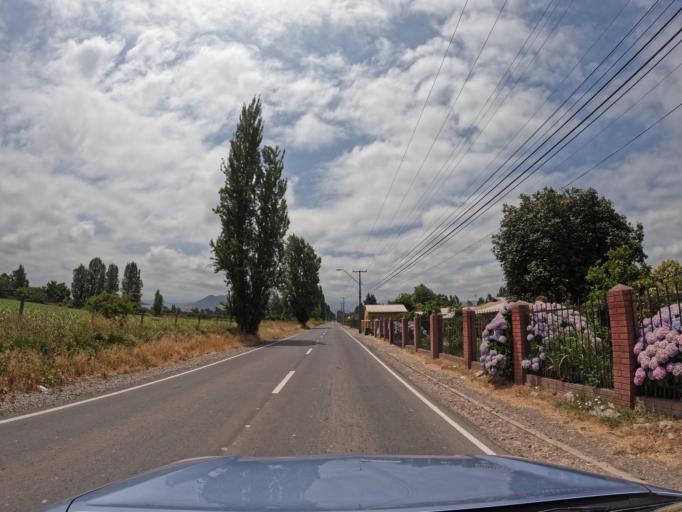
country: CL
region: O'Higgins
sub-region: Provincia de Colchagua
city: Chimbarongo
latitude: -34.7283
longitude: -70.9979
